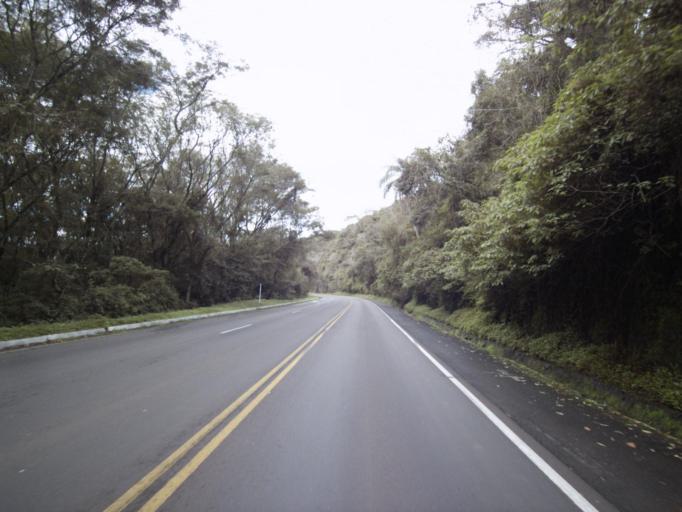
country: BR
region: Santa Catarina
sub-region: Concordia
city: Concordia
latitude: -27.3639
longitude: -51.9976
